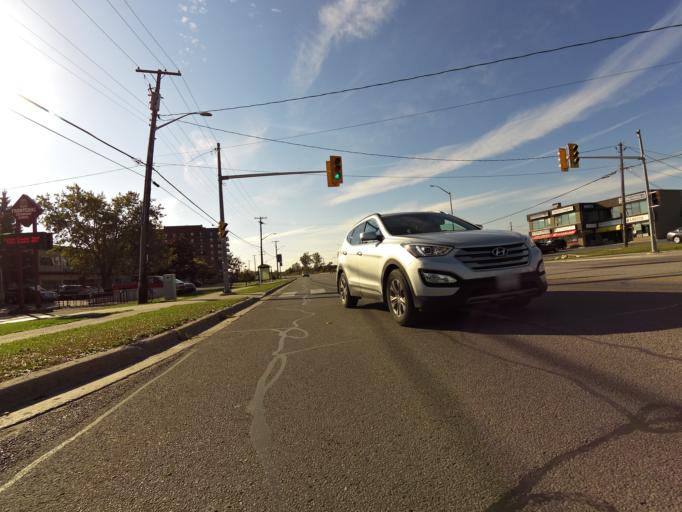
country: CA
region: Ontario
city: Kingston
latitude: 44.2376
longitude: -76.5766
